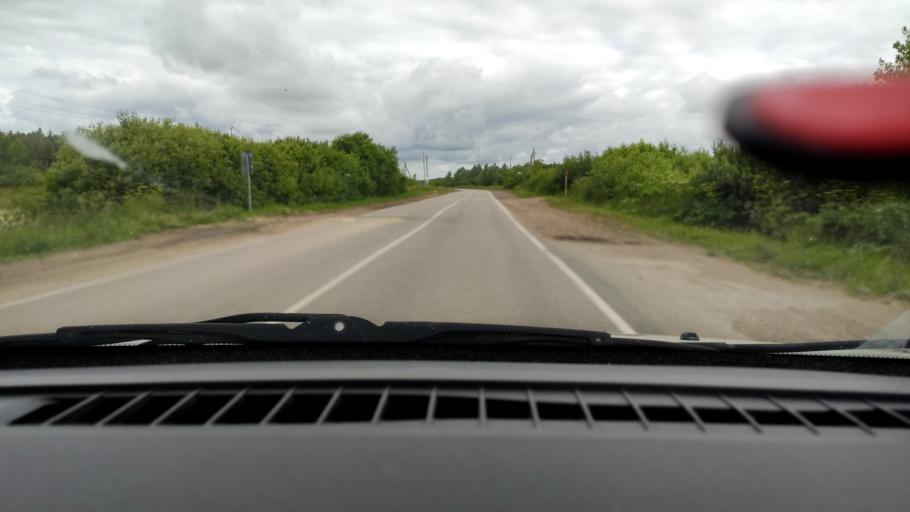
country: RU
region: Perm
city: Chaykovskaya
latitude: 58.0873
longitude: 55.6129
